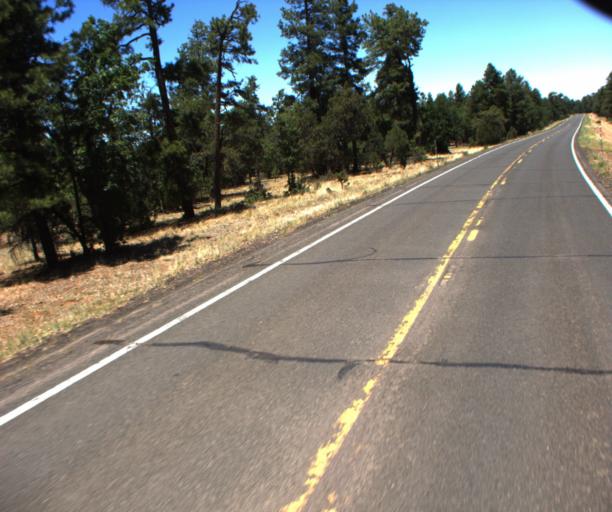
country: US
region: Arizona
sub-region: Gila County
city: Star Valley
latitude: 34.6592
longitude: -111.1093
